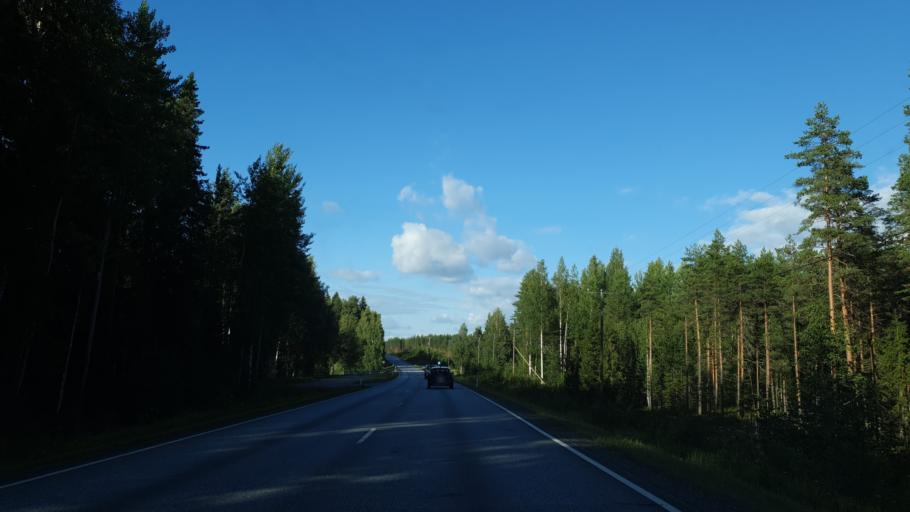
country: FI
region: North Karelia
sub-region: Joensuu
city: Outokumpu
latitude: 62.5397
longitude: 29.1211
